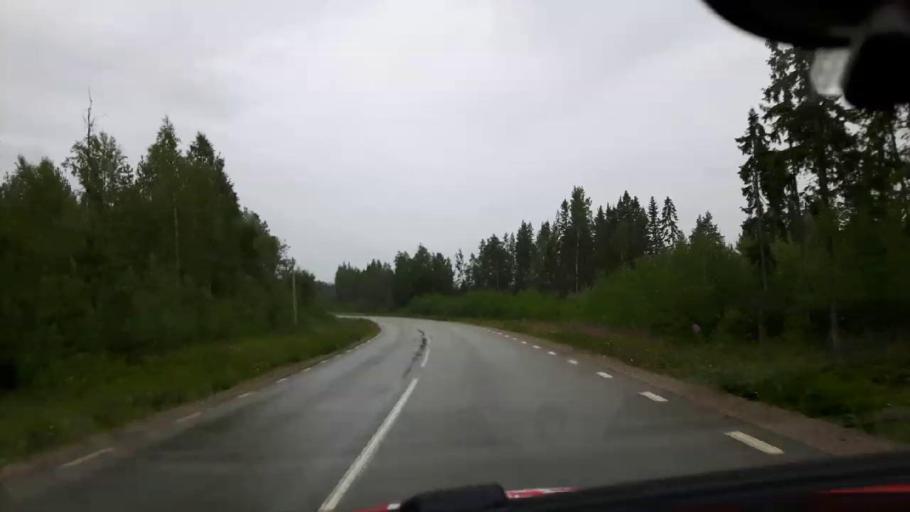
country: SE
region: Jaemtland
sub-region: OEstersunds Kommun
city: Brunflo
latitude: 62.7864
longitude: 15.0071
